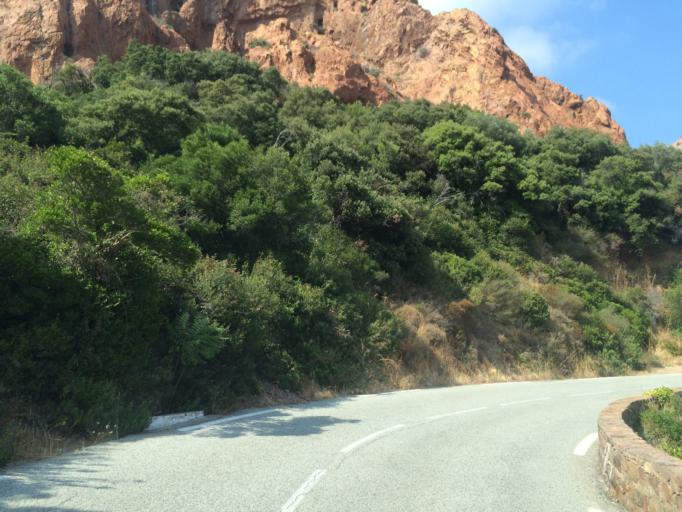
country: FR
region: Provence-Alpes-Cote d'Azur
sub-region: Departement des Alpes-Maritimes
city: Theoule-sur-Mer
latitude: 43.4455
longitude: 6.9038
